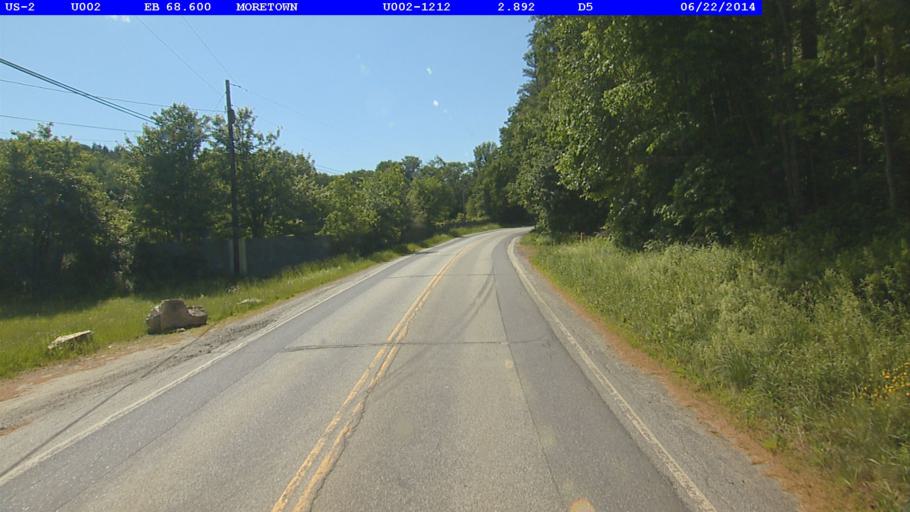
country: US
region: Vermont
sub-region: Washington County
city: Waterbury
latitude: 44.3106
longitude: -72.6984
